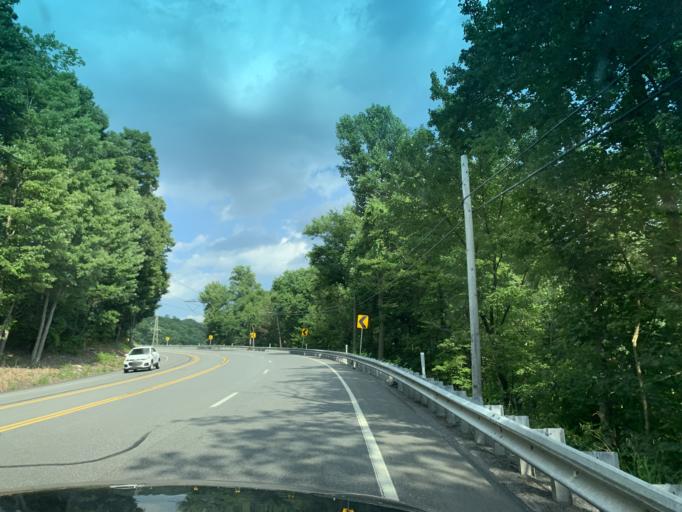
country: US
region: Pennsylvania
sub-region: Schuylkill County
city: Girardville
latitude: 40.7766
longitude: -76.2752
